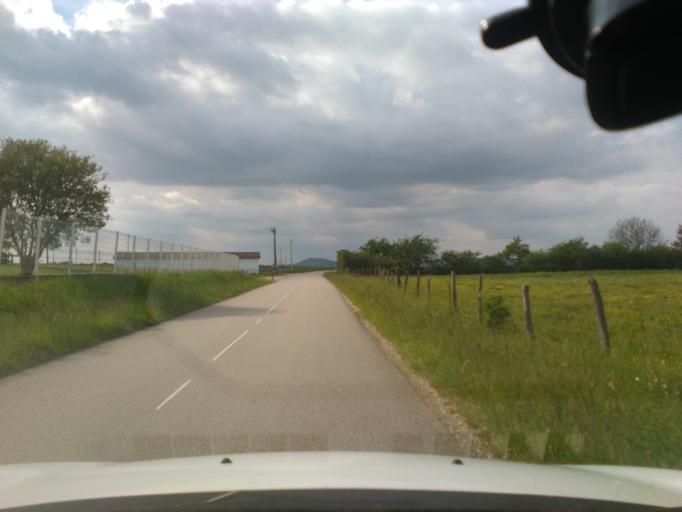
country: FR
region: Lorraine
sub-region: Departement des Vosges
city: Mirecourt
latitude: 48.3203
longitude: 6.1197
